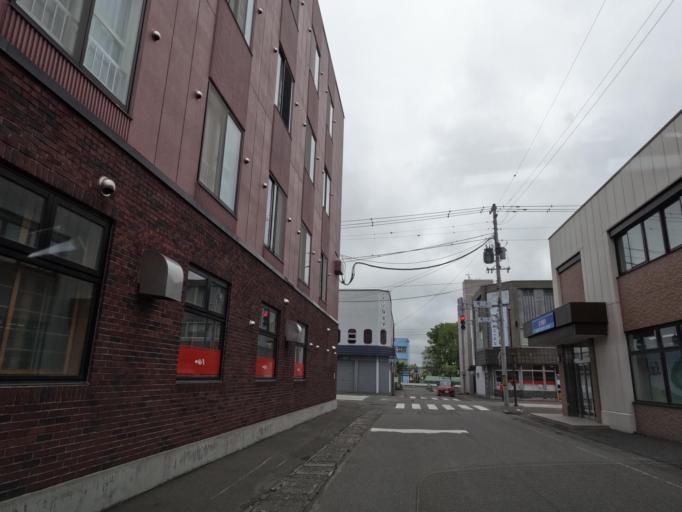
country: JP
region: Hokkaido
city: Tobetsu
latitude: 43.2218
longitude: 141.5172
